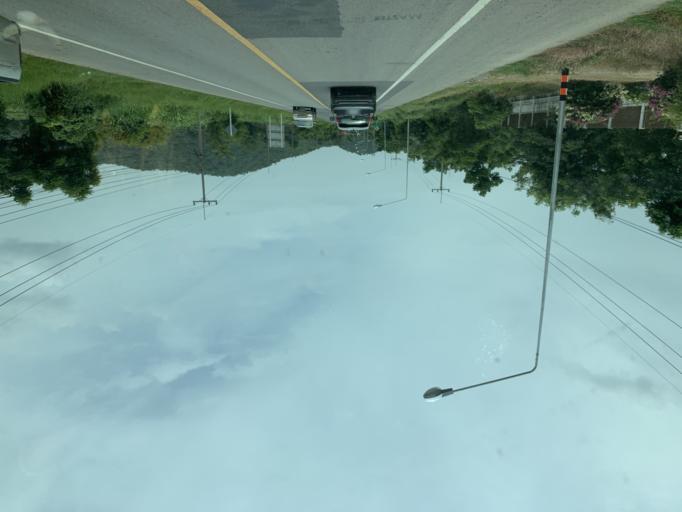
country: TH
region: Uthai Thani
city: Uthai Thani
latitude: 15.4108
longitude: 100.0048
